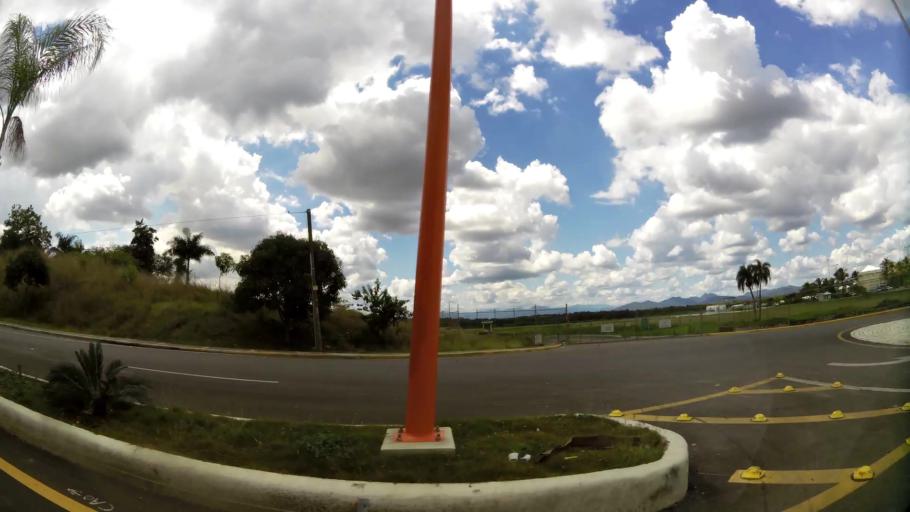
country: DO
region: Nacional
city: Santo Domingo
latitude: 18.5739
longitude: -69.9807
